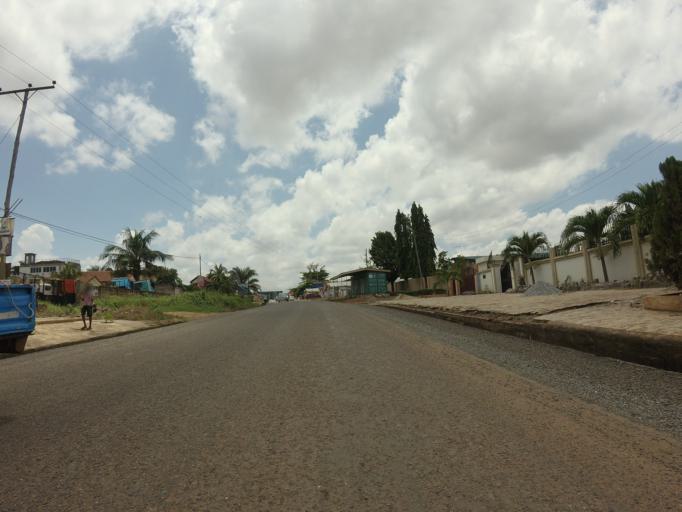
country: GH
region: Greater Accra
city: Medina Estates
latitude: 5.6809
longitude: -0.1954
